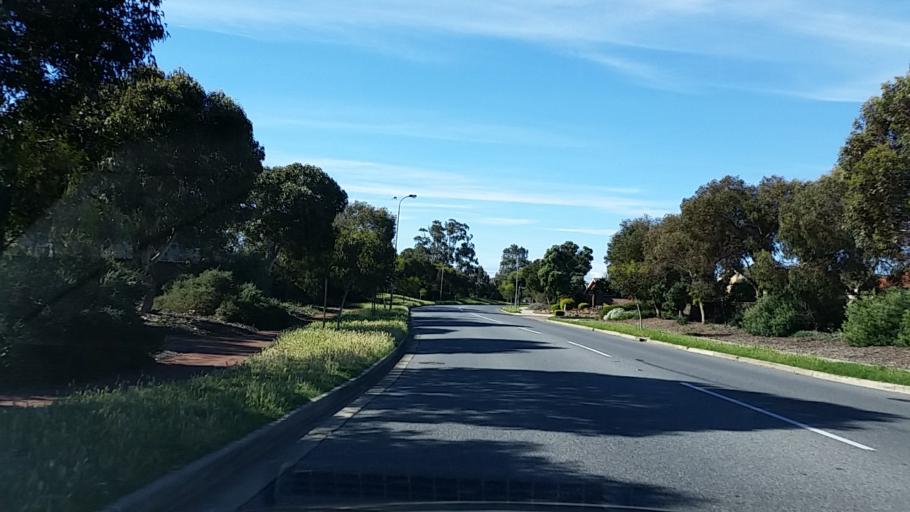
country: AU
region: South Australia
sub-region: Charles Sturt
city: West Lakes Shore
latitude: -34.8713
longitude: 138.4884
